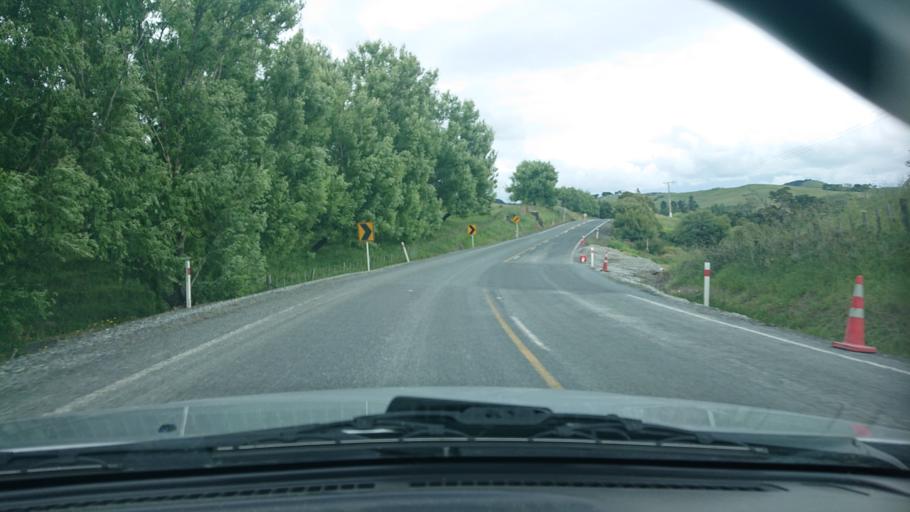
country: NZ
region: Auckland
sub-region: Auckland
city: Wellsford
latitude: -36.3730
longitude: 174.4547
